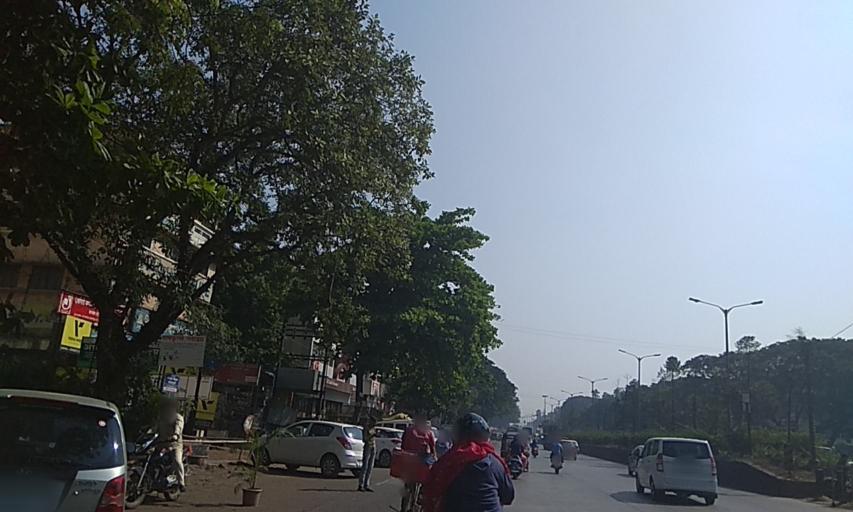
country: IN
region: Maharashtra
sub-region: Pune Division
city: Pune
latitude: 18.5005
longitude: 73.9422
